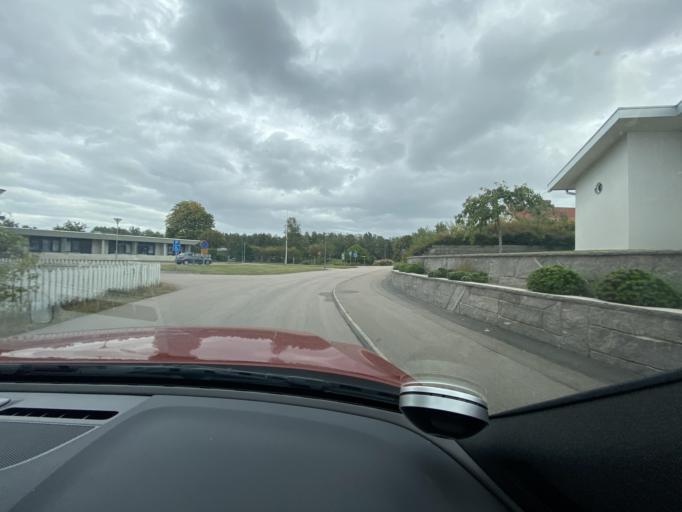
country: SE
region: Kronoberg
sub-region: Markaryds Kommun
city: Markaryd
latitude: 56.4616
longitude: 13.6039
